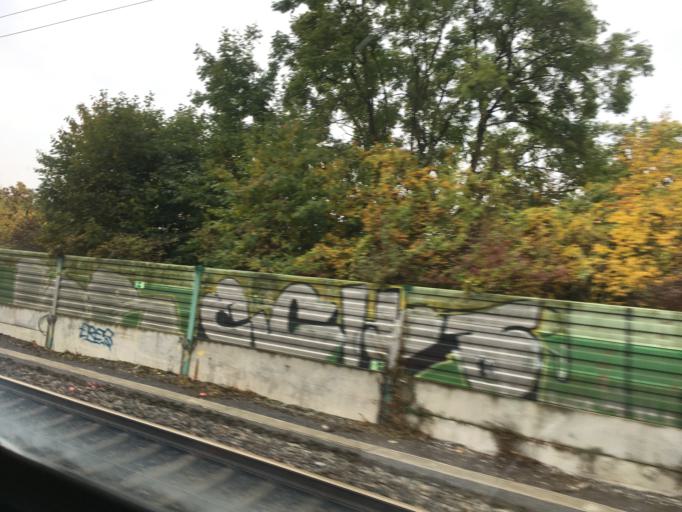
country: DE
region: North Rhine-Westphalia
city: Lengerich
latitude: 52.1804
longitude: 7.8716
